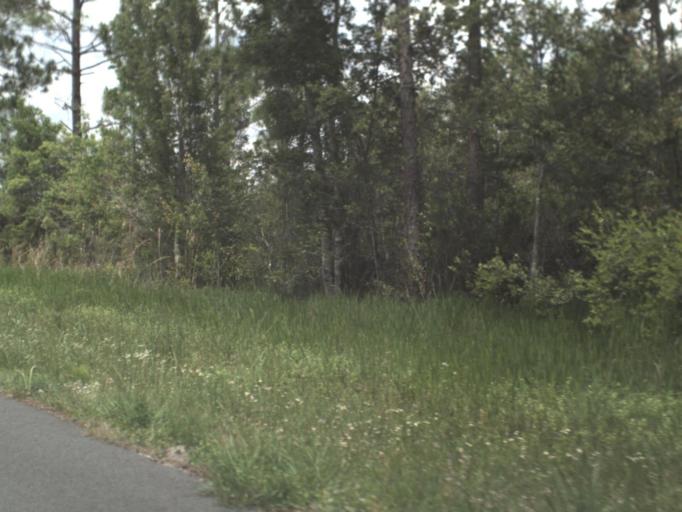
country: US
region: Florida
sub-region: Hamilton County
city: Jasper
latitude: 30.5761
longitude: -82.6795
